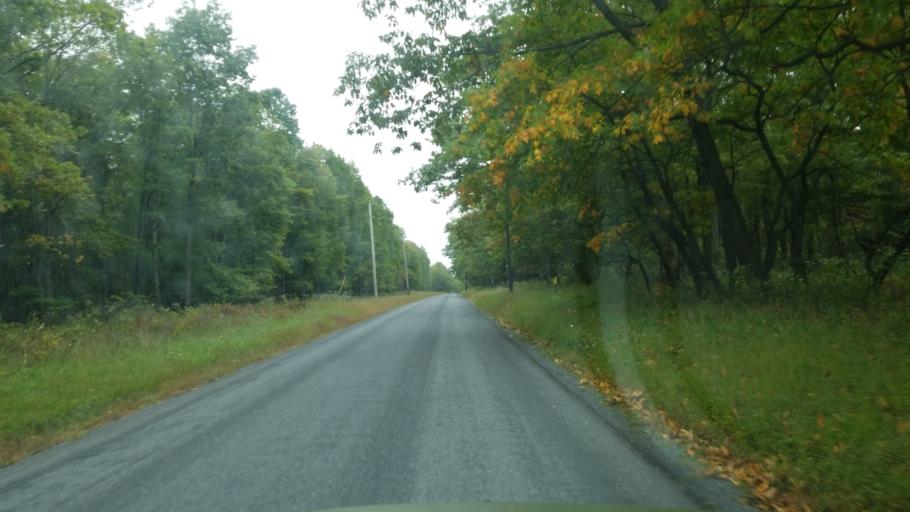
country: US
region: Pennsylvania
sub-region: Clearfield County
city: Curwensville
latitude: 41.0353
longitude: -78.5616
